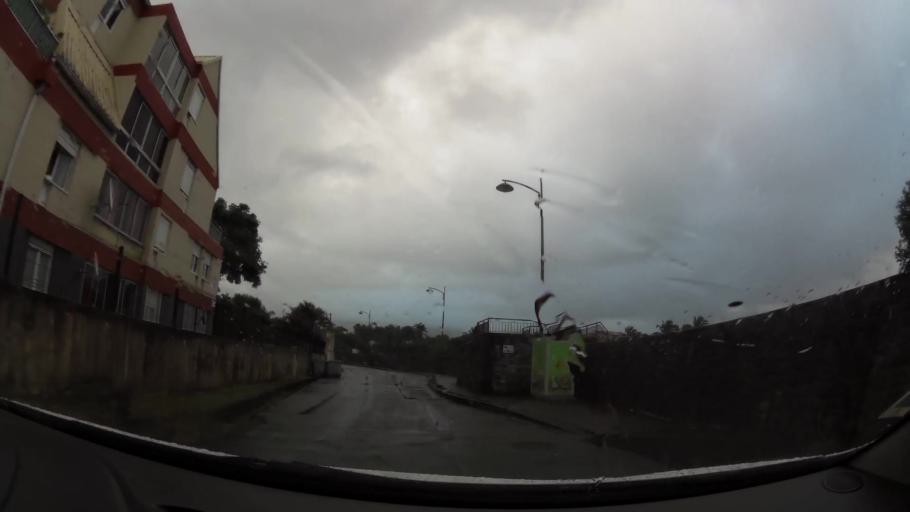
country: RE
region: Reunion
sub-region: Reunion
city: Saint-Benoit
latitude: -21.0364
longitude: 55.7146
